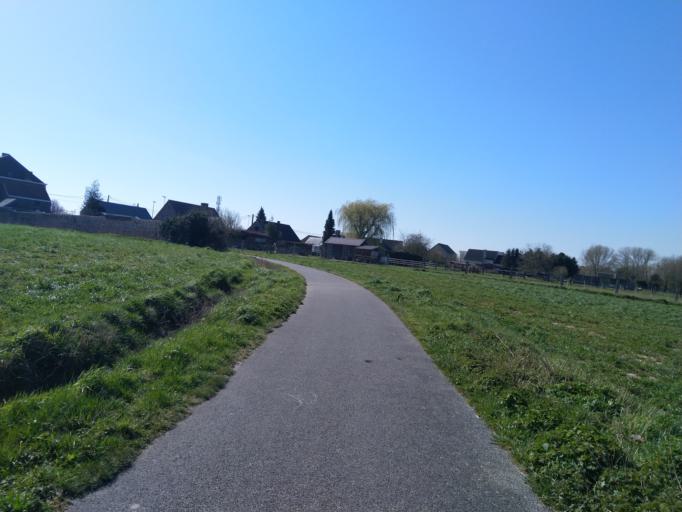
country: BE
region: Wallonia
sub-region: Province du Hainaut
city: Soignies
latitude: 50.5677
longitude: 3.9984
